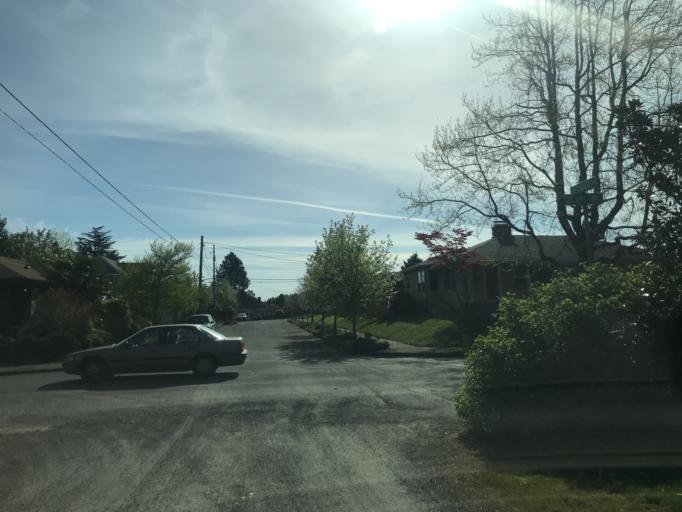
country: US
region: Oregon
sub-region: Multnomah County
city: Lents
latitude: 45.5023
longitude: -122.5969
